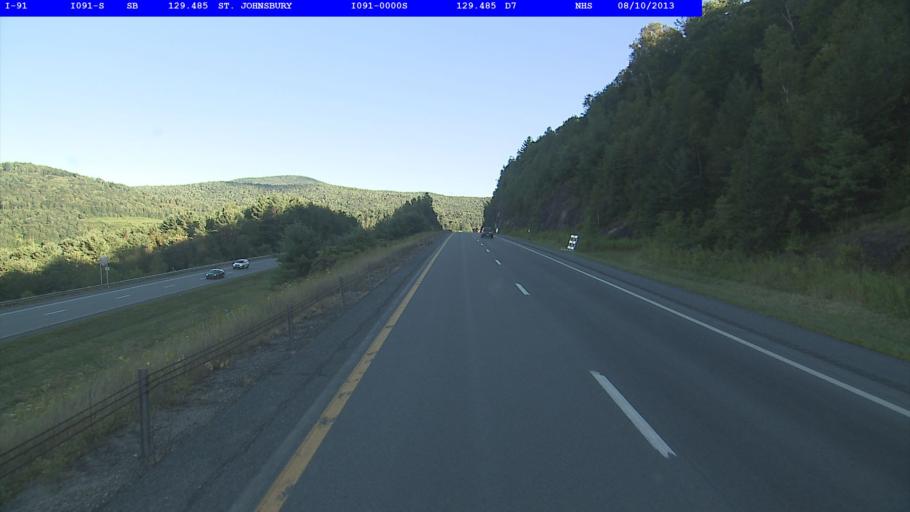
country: US
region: Vermont
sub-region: Caledonia County
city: Saint Johnsbury
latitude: 44.4121
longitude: -72.0290
